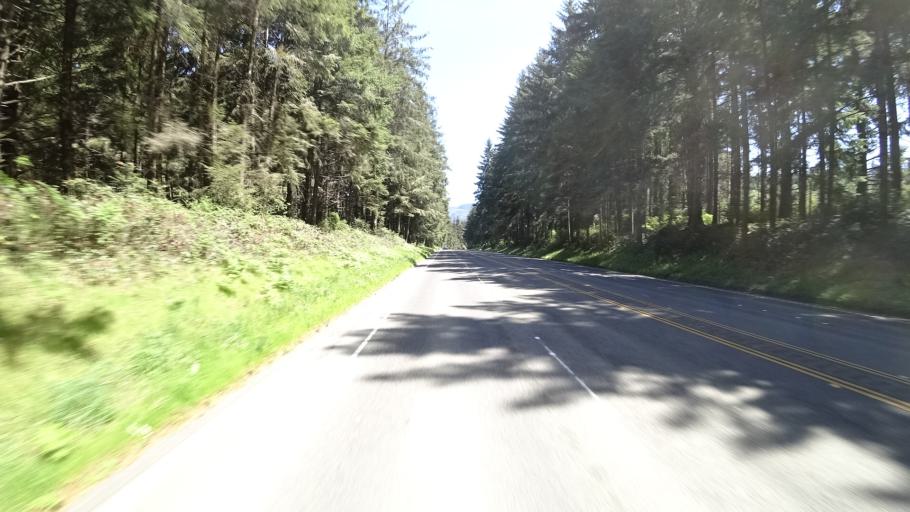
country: US
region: California
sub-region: Humboldt County
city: Westhaven-Moonstone
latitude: 41.1572
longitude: -124.1252
